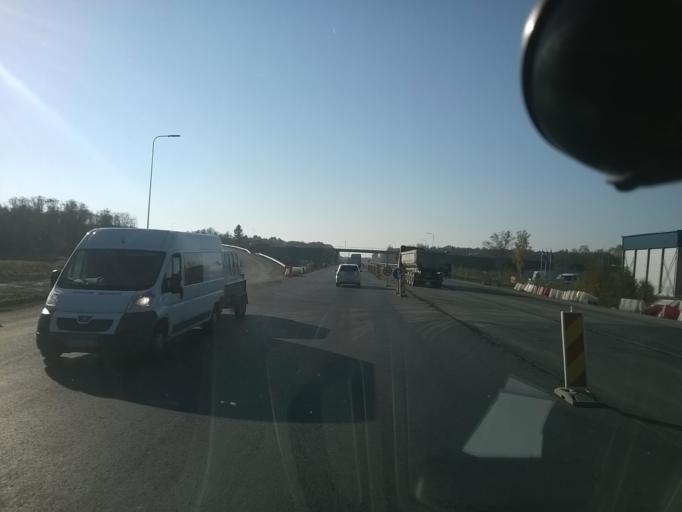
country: EE
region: Harju
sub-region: Rae vald
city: Jueri
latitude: 59.3744
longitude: 24.9119
